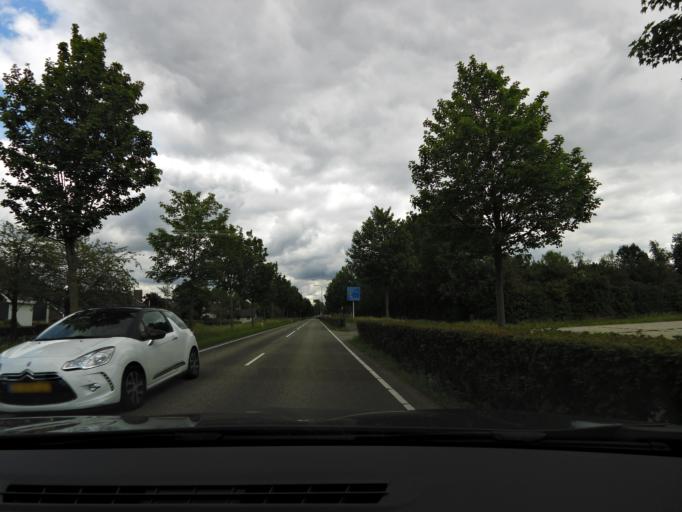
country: NL
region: South Holland
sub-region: Gemeente Oud-Beijerland
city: Oud-Beijerland
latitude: 51.8141
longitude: 4.4087
